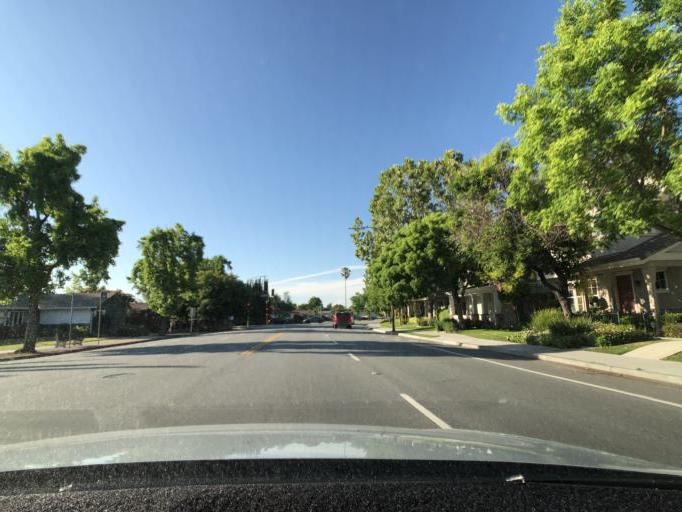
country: US
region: California
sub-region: Santa Clara County
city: Cambrian Park
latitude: 37.2665
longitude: -121.9224
